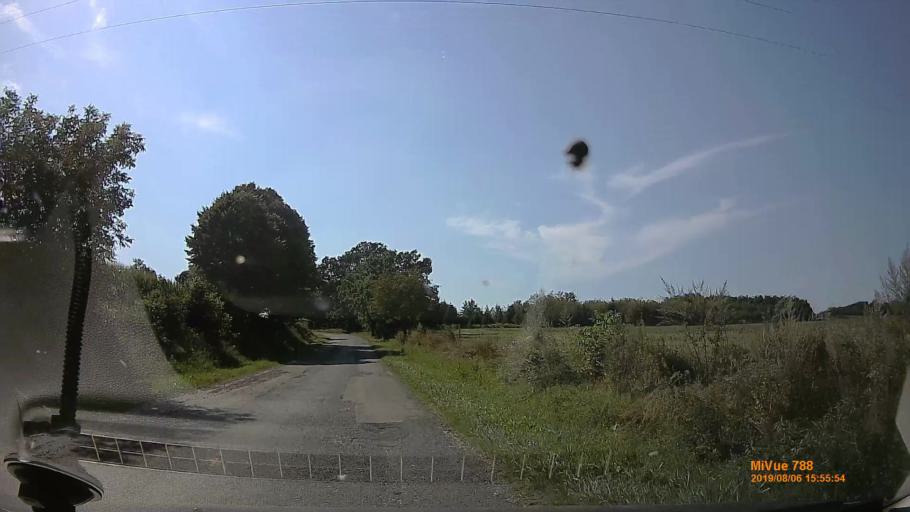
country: HU
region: Somogy
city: Csurgo
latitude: 46.2910
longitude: 17.0152
